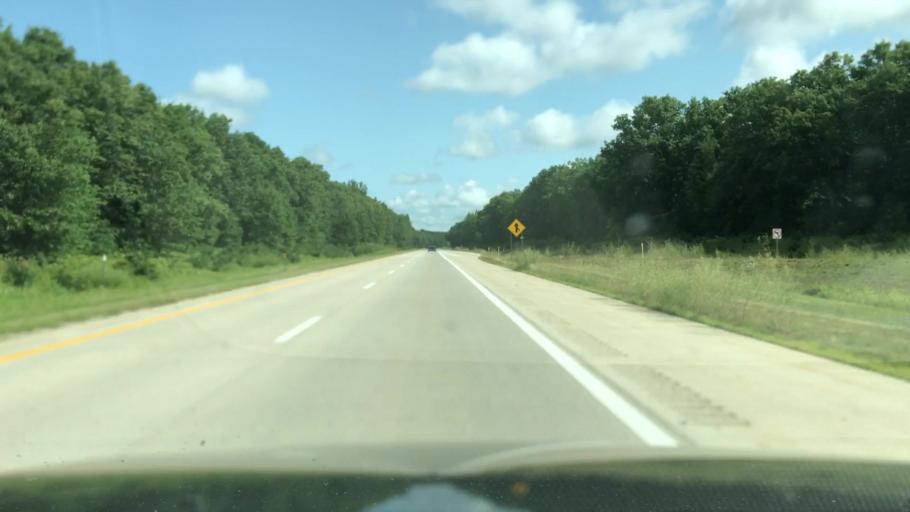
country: US
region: Michigan
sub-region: Montcalm County
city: Howard City
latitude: 43.3987
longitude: -85.5122
